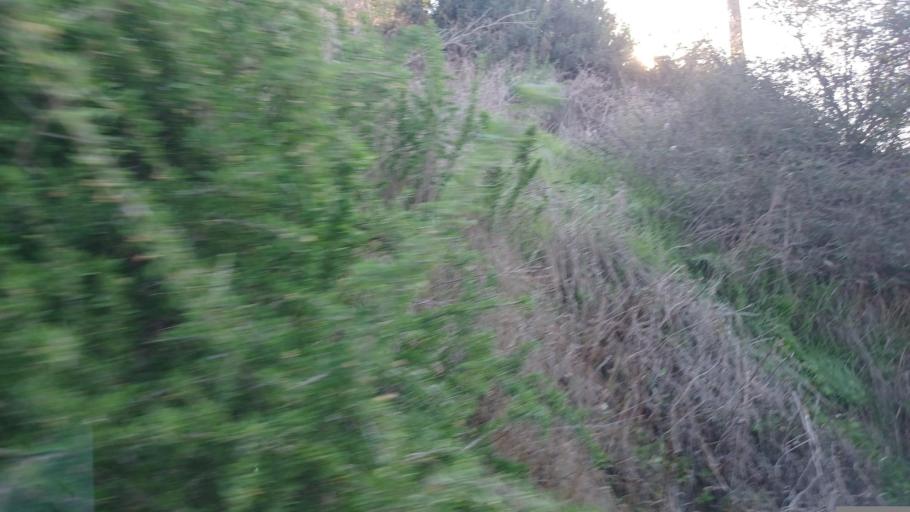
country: CY
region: Pafos
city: Kissonerga
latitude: 34.8348
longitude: 32.3950
